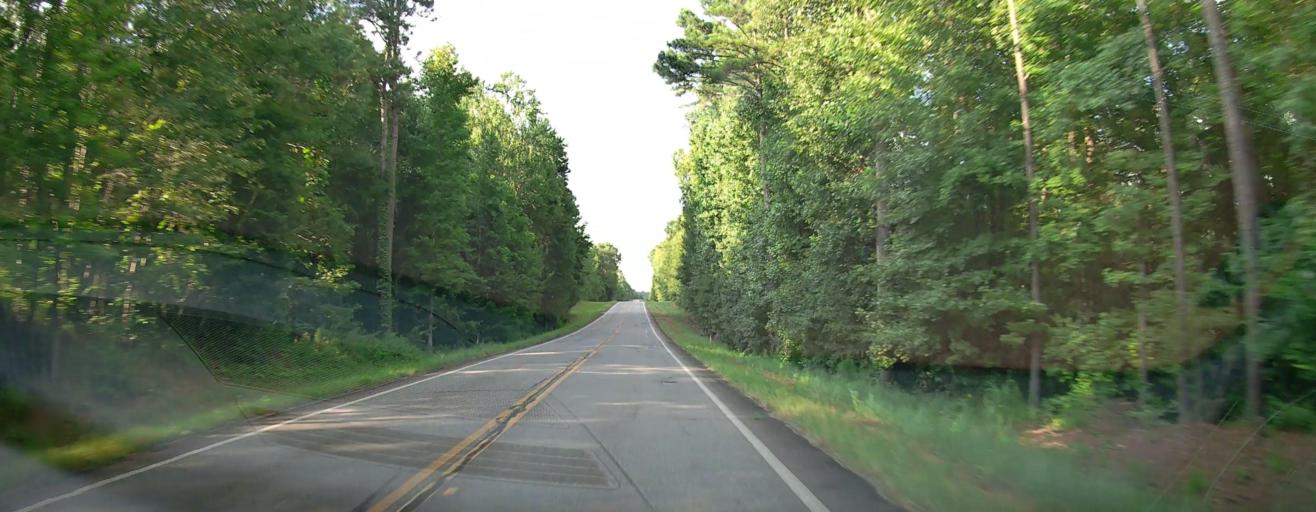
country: US
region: Georgia
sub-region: Crawford County
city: Knoxville
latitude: 32.8275
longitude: -84.0193
